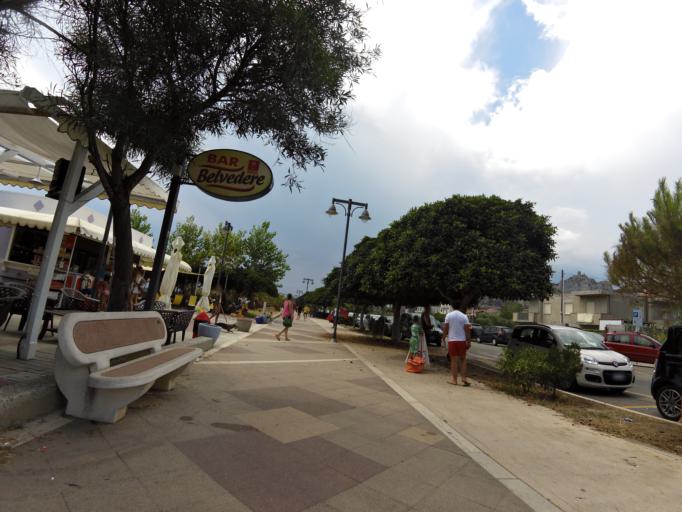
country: IT
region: Calabria
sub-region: Provincia di Reggio Calabria
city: Roccella Ionica
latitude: 38.3246
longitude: 16.4167
